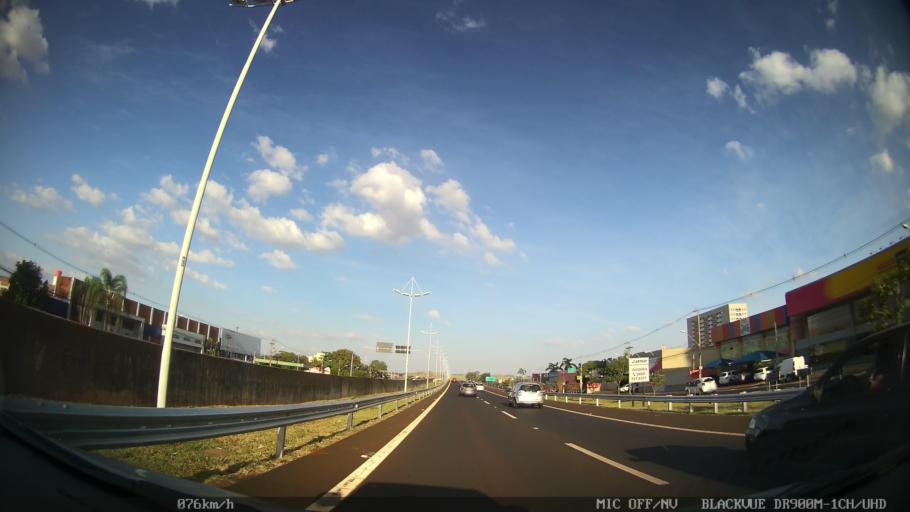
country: BR
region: Sao Paulo
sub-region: Ribeirao Preto
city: Ribeirao Preto
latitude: -21.1983
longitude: -47.7695
